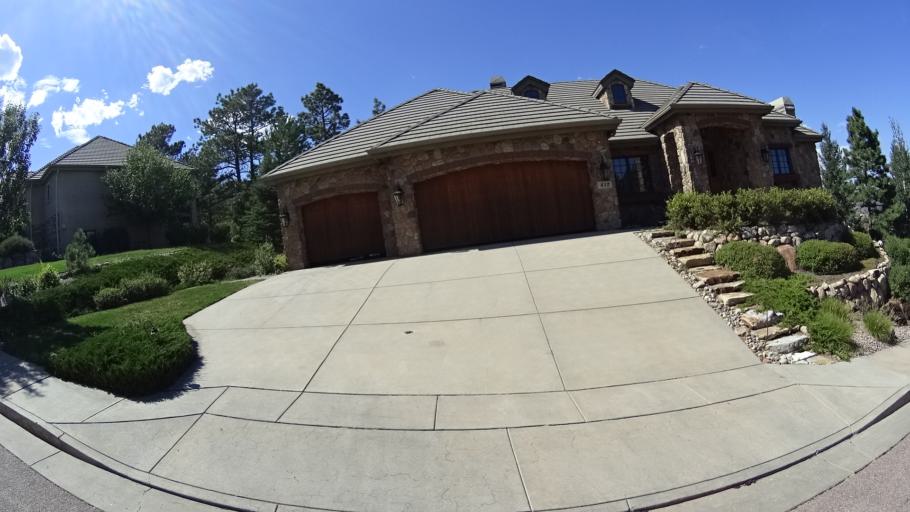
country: US
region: Colorado
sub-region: El Paso County
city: Colorado Springs
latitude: 38.8156
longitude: -104.8753
